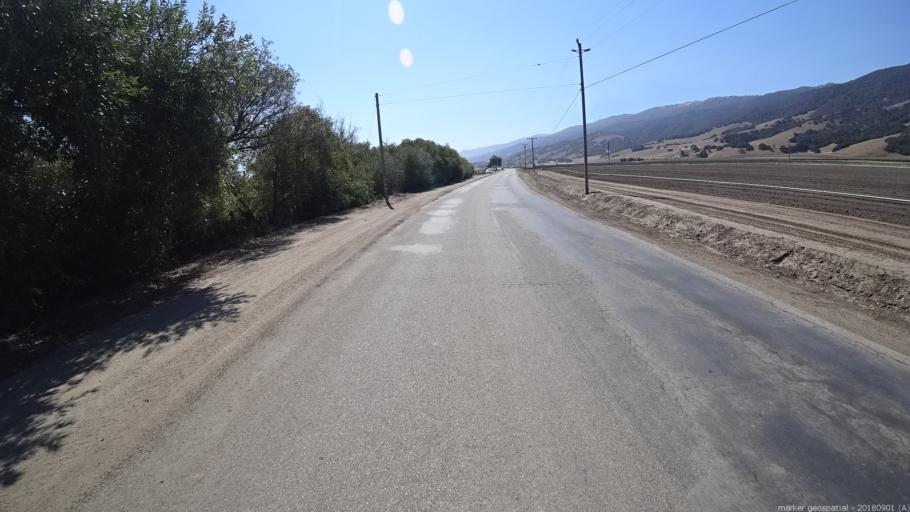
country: US
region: California
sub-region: Monterey County
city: Chualar
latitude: 36.5487
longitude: -121.5470
